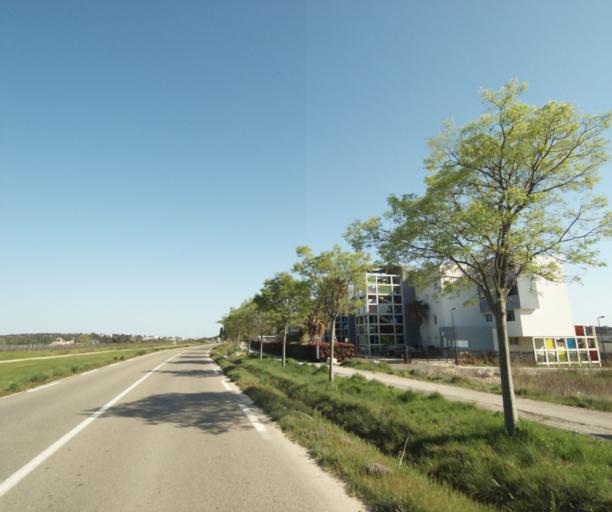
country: FR
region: Languedoc-Roussillon
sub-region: Departement de l'Herault
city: Jacou
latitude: 43.6703
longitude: 3.9153
